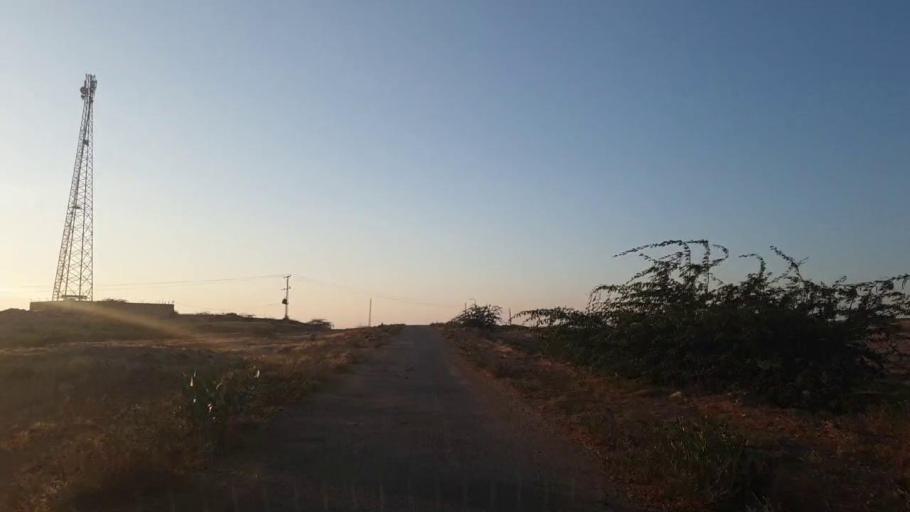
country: PK
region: Sindh
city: Gharo
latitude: 25.1654
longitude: 67.6717
